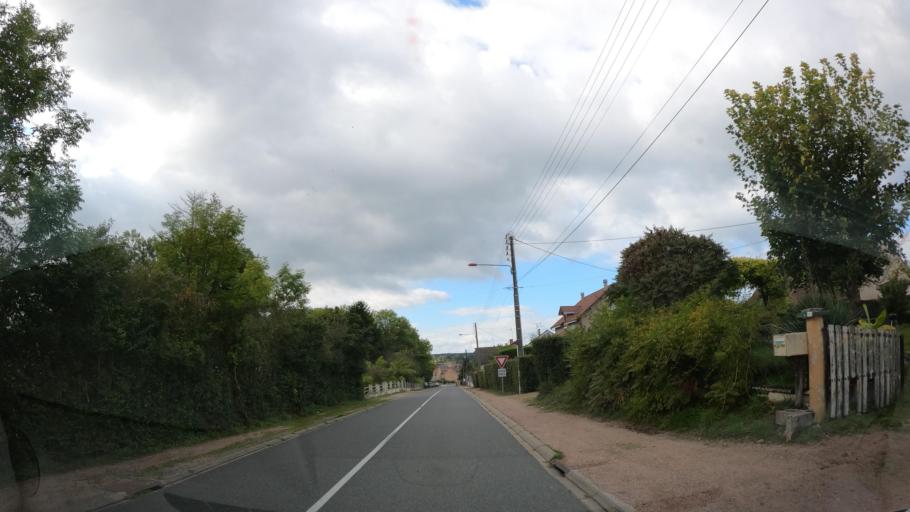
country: FR
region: Auvergne
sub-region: Departement de l'Allier
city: Lapalisse
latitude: 46.3784
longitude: 3.5960
